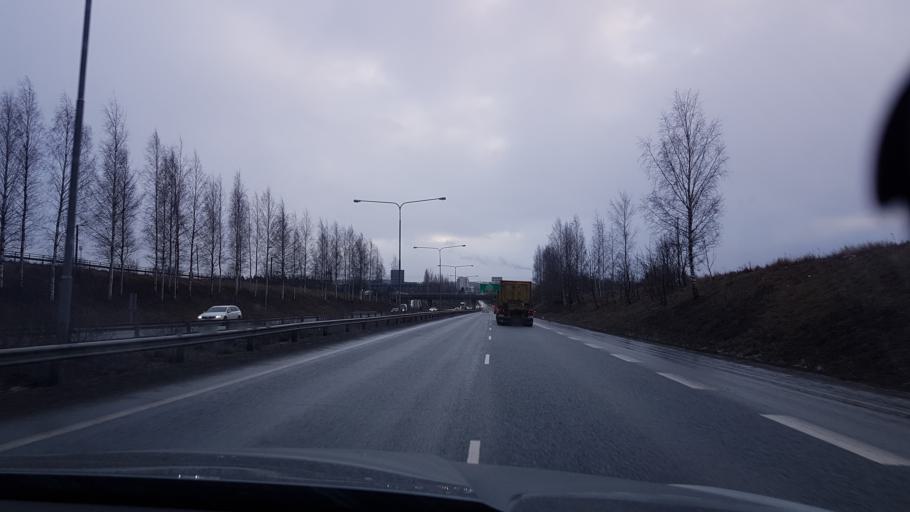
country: FI
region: Pirkanmaa
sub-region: Tampere
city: Tampere
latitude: 61.4860
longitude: 23.8738
